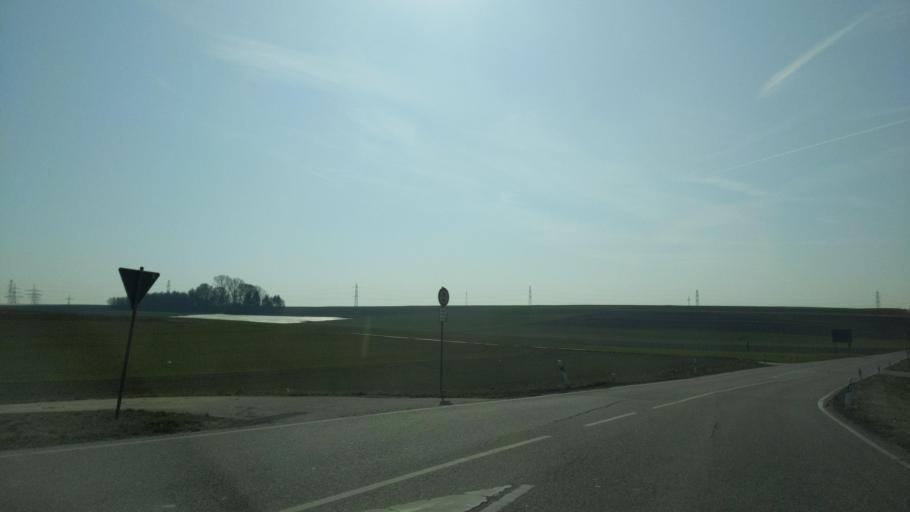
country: DE
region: Baden-Wuerttemberg
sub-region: Regierungsbezirk Stuttgart
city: Schwieberdingen
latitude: 48.8798
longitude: 9.0976
